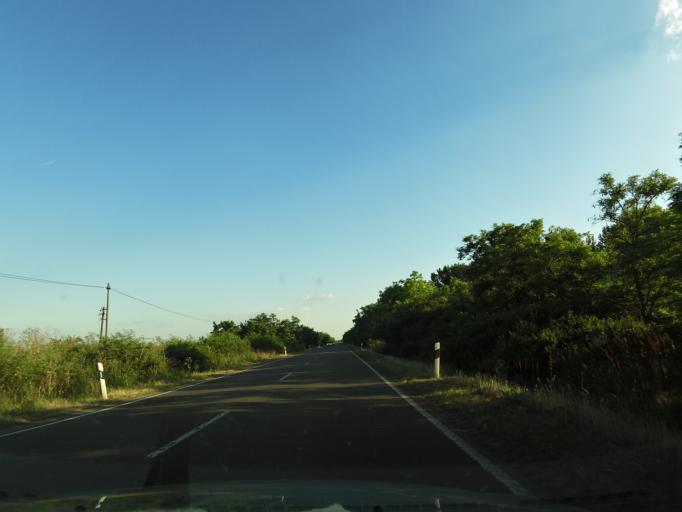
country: HU
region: Jasz-Nagykun-Szolnok
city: Tiszafoldvar
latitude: 46.9966
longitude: 20.2836
